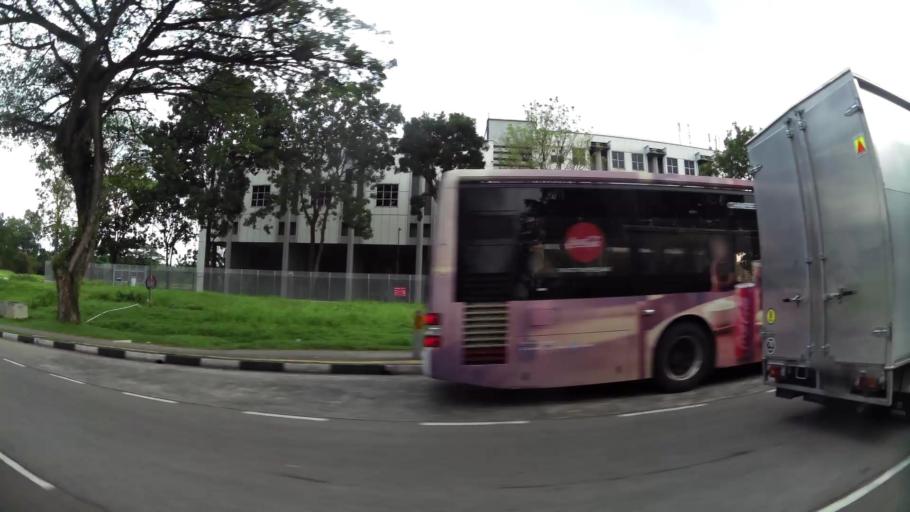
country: MY
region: Johor
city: Kampung Pasir Gudang Baru
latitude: 1.4528
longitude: 103.8311
